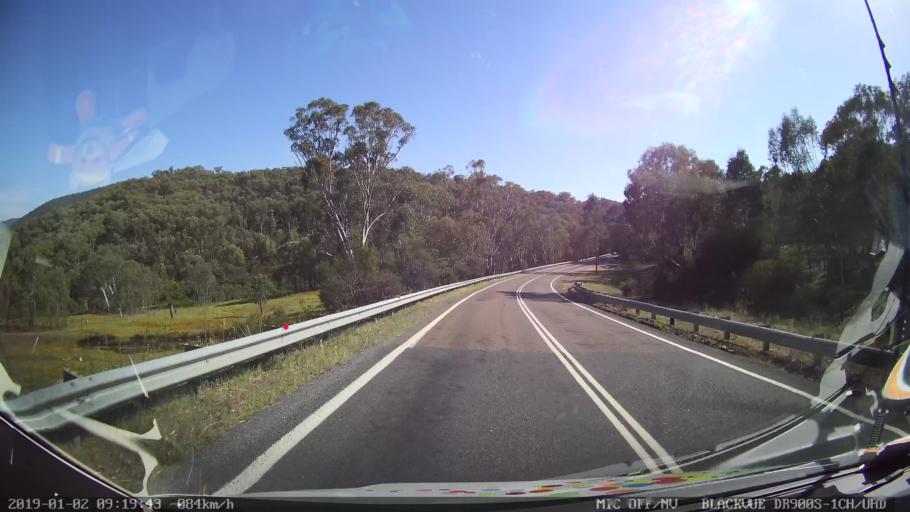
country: AU
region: New South Wales
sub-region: Tumut Shire
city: Tumut
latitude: -35.4190
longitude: 148.2768
